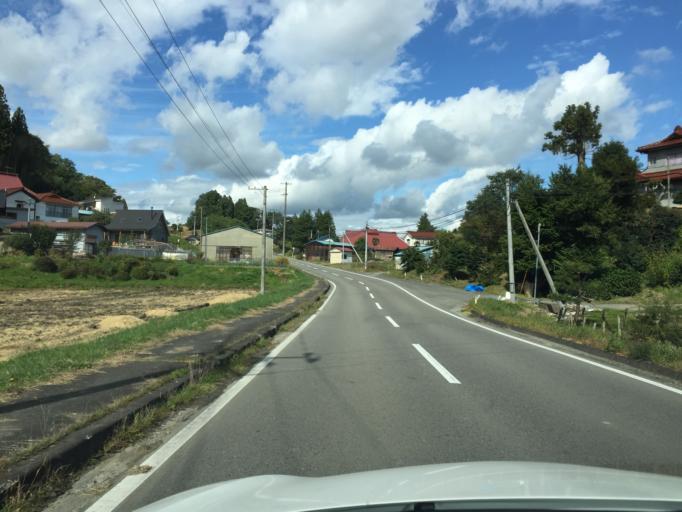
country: JP
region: Fukushima
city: Funehikimachi-funehiki
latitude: 37.4206
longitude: 140.5498
